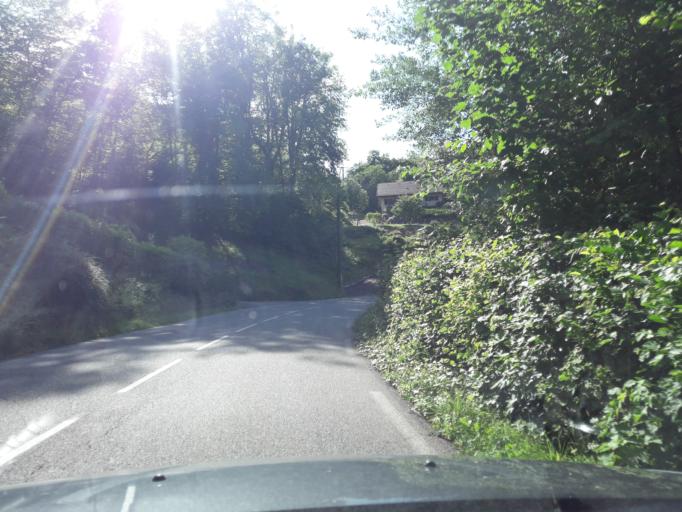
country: FR
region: Rhone-Alpes
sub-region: Departement de la Savoie
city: Vimines
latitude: 45.5372
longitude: 5.8106
